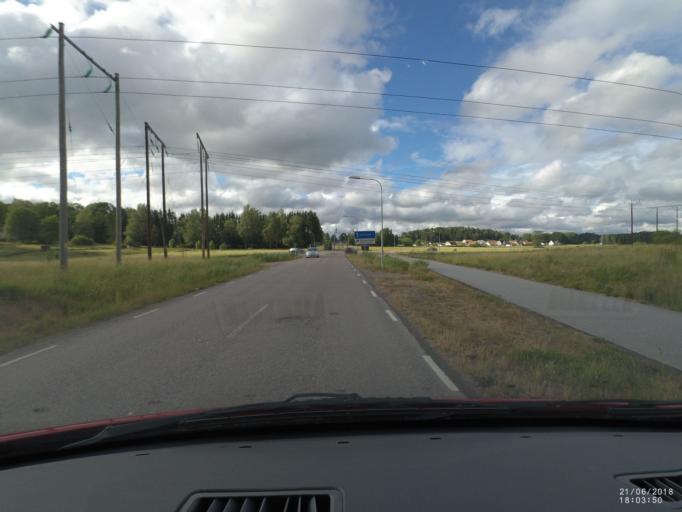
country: SE
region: Soedermanland
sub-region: Nykopings Kommun
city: Nykoping
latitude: 58.7701
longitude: 17.0071
